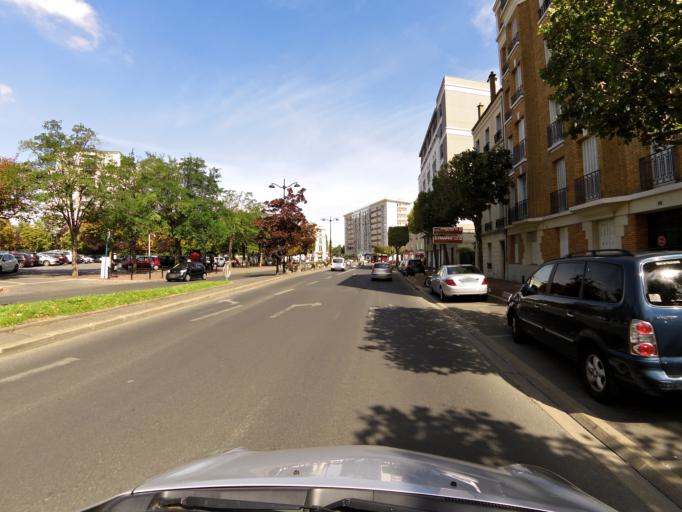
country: FR
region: Ile-de-France
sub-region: Departement du Val-de-Marne
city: Joinville-le-Pont
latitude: 48.8163
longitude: 2.4676
